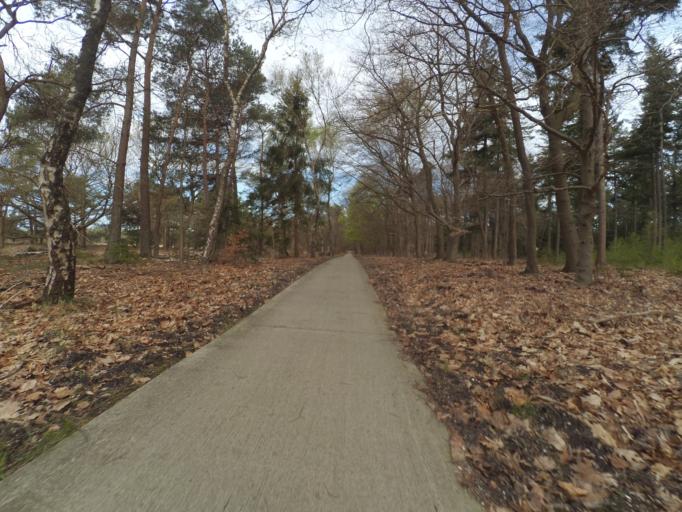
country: NL
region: Gelderland
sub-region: Gemeente Nunspeet
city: Nunspeet
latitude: 52.3416
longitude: 5.7757
